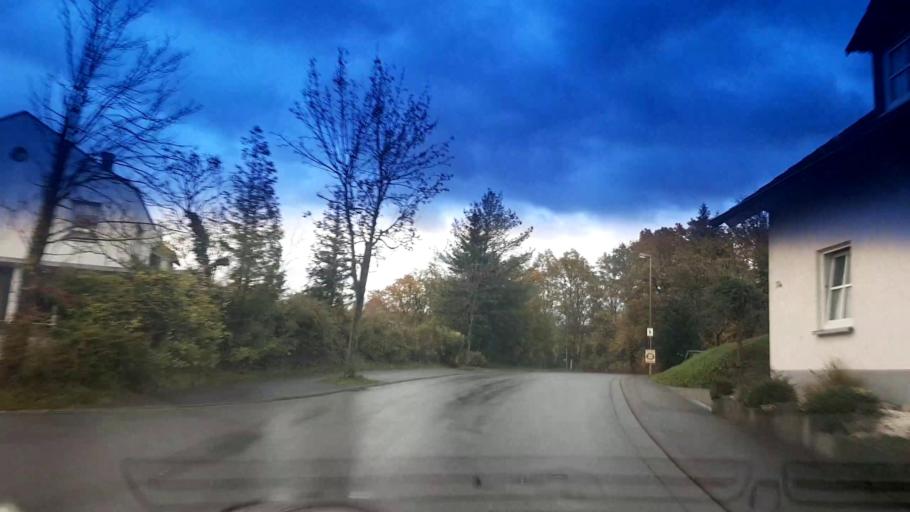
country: DE
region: Bavaria
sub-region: Upper Franconia
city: Viereth-Trunstadt
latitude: 49.9230
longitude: 10.7713
